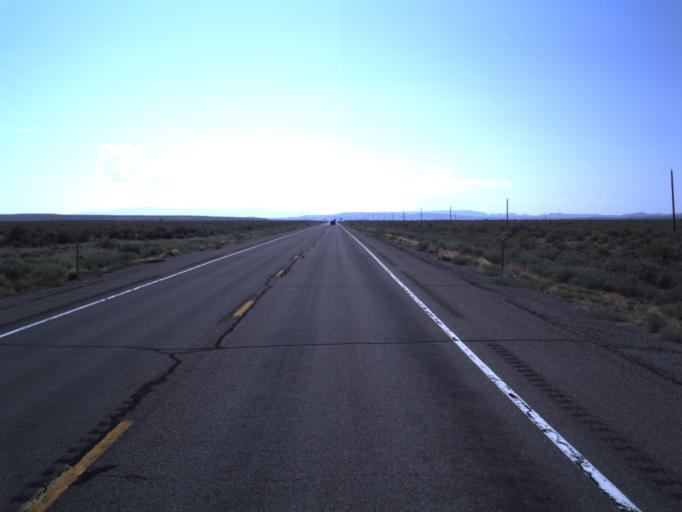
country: US
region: Utah
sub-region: San Juan County
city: Blanding
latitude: 37.1950
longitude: -109.5994
